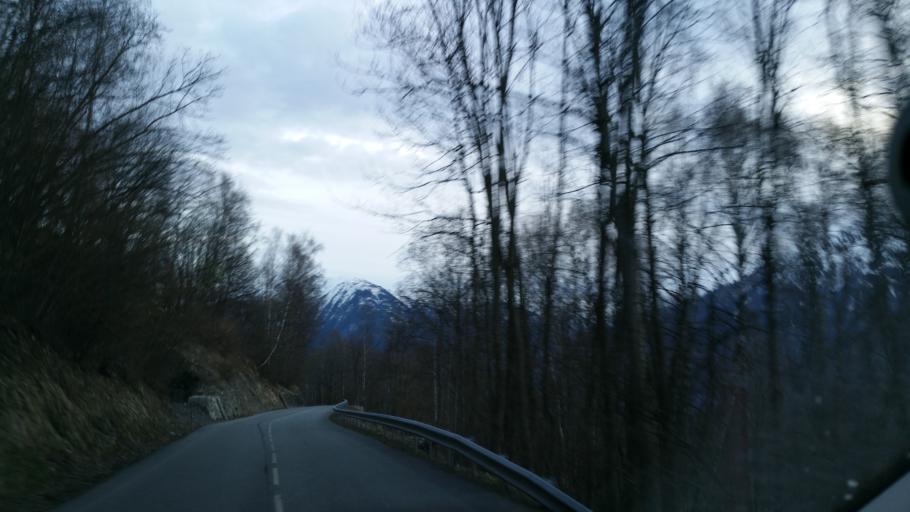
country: FR
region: Rhone-Alpes
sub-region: Departement de la Savoie
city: La Chambre
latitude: 45.3949
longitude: 6.3358
